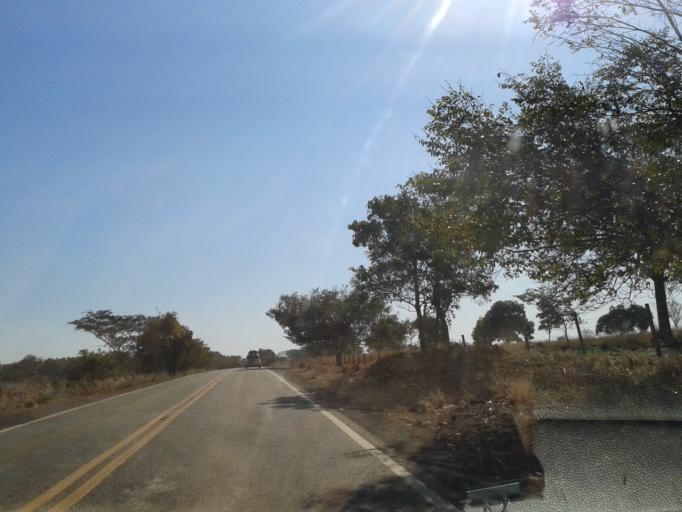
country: BR
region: Goias
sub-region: Mozarlandia
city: Mozarlandia
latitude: -14.5643
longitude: -50.4984
